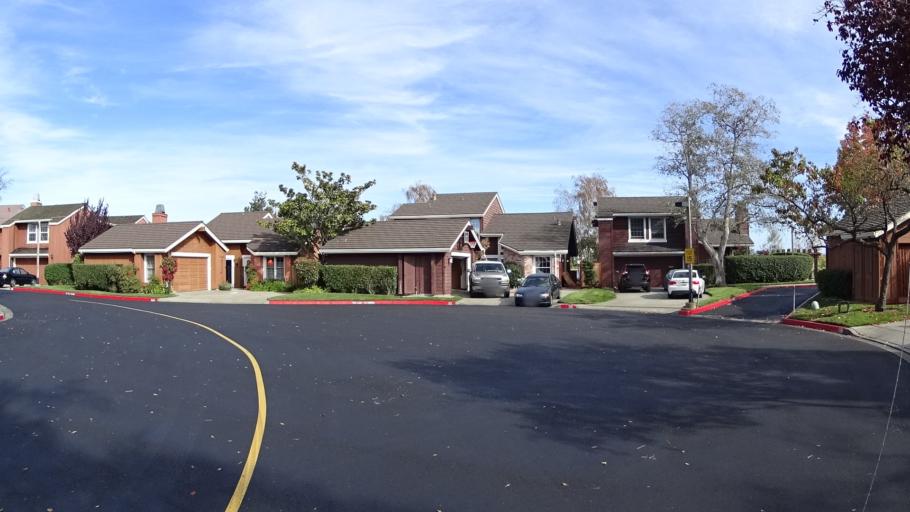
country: US
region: California
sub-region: San Mateo County
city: Redwood Shores
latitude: 37.5459
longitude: -122.2580
